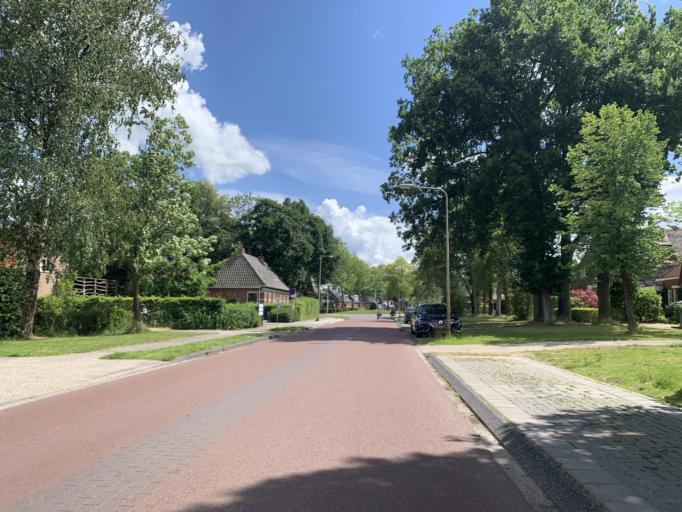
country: NL
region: Groningen
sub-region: Gemeente Haren
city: Haren
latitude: 53.1761
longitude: 6.6070
